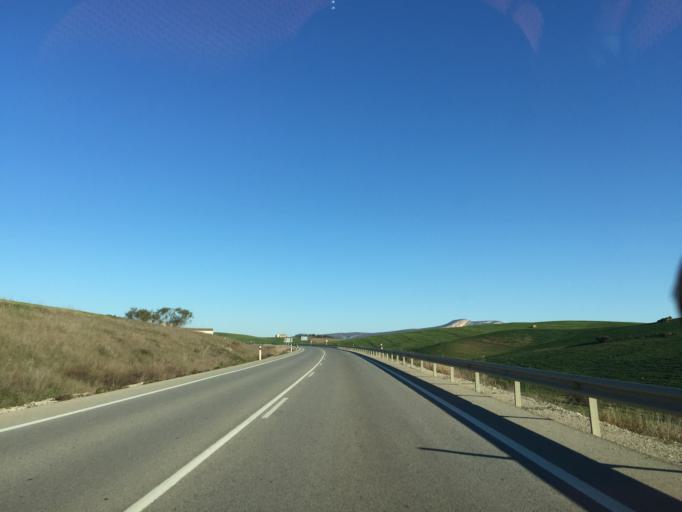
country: ES
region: Andalusia
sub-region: Provincia de Malaga
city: Ardales
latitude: 36.9177
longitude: -4.8423
